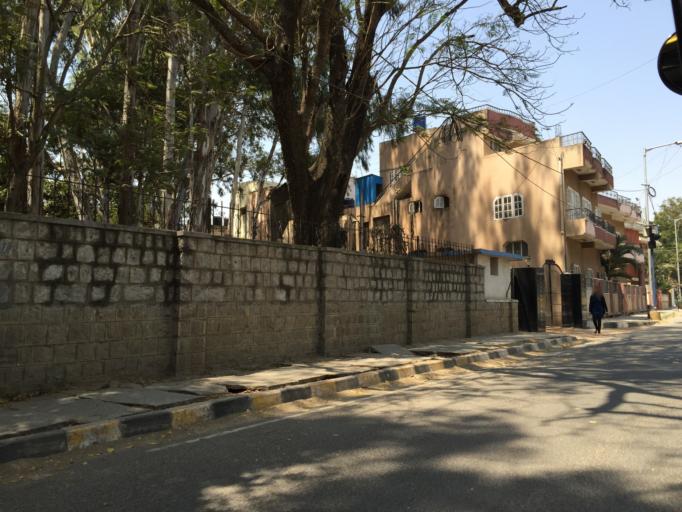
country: IN
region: Karnataka
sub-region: Bangalore Urban
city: Bangalore
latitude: 12.9941
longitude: 77.6181
